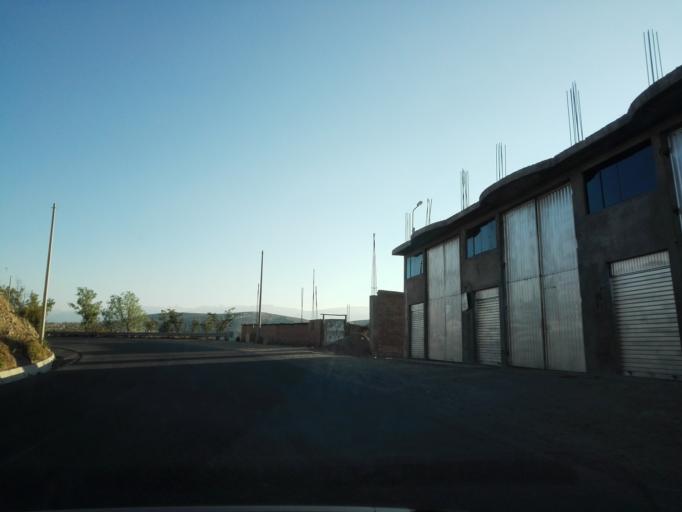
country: PE
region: Ayacucho
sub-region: Provincia de Huamanga
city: Ayacucho
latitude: -13.1377
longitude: -74.2224
